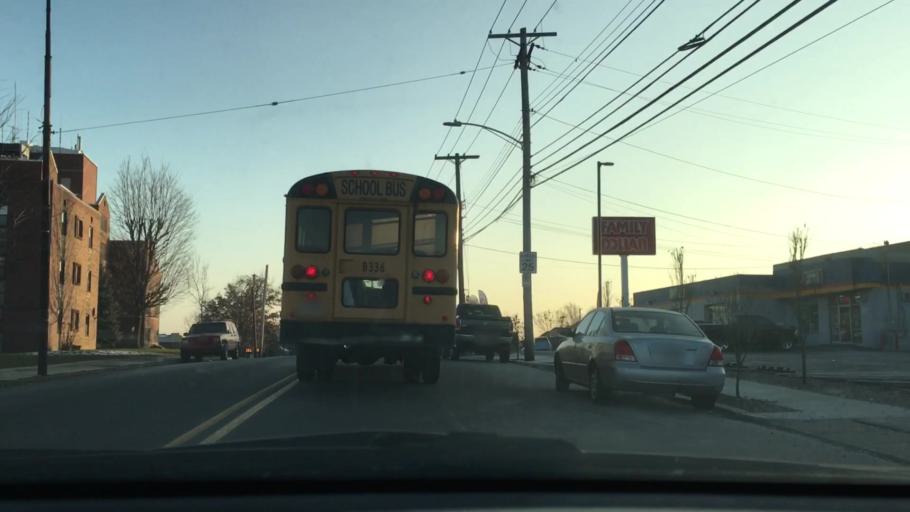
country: US
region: Pennsylvania
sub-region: Allegheny County
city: Mount Oliver
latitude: 40.3929
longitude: -79.9866
